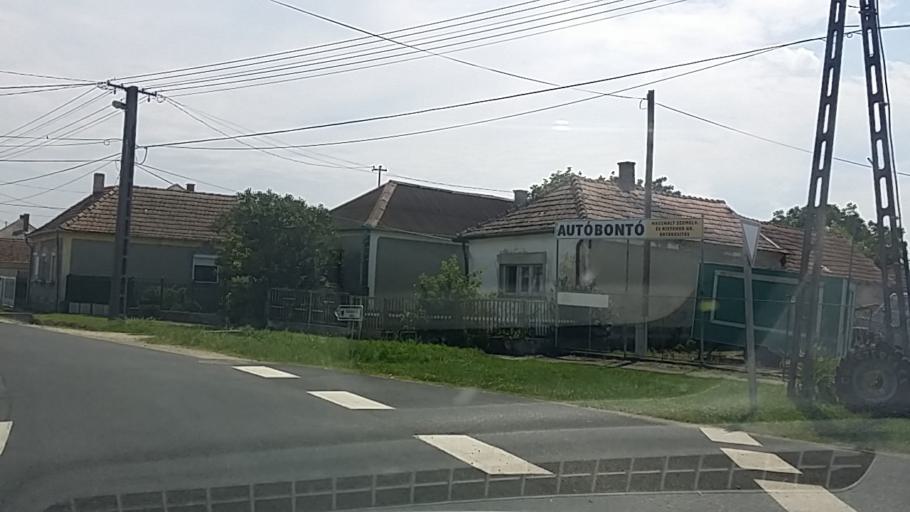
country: HU
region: Zala
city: Letenye
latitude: 46.4208
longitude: 16.7441
